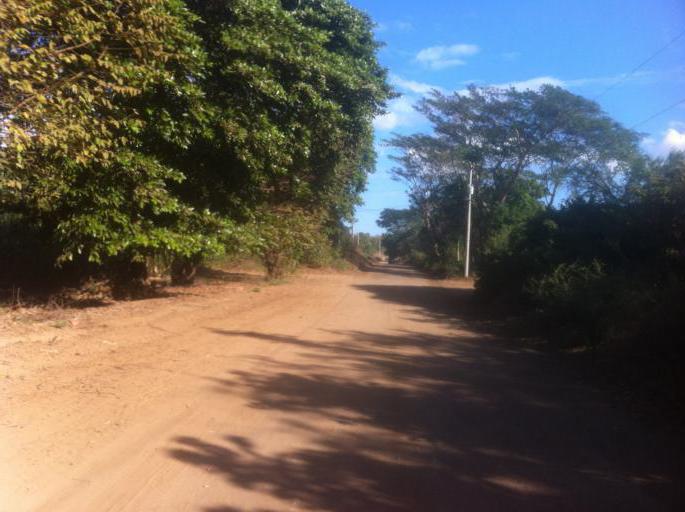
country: NI
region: Managua
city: Carlos Fonseca Amador
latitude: 11.8932
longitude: -86.5858
